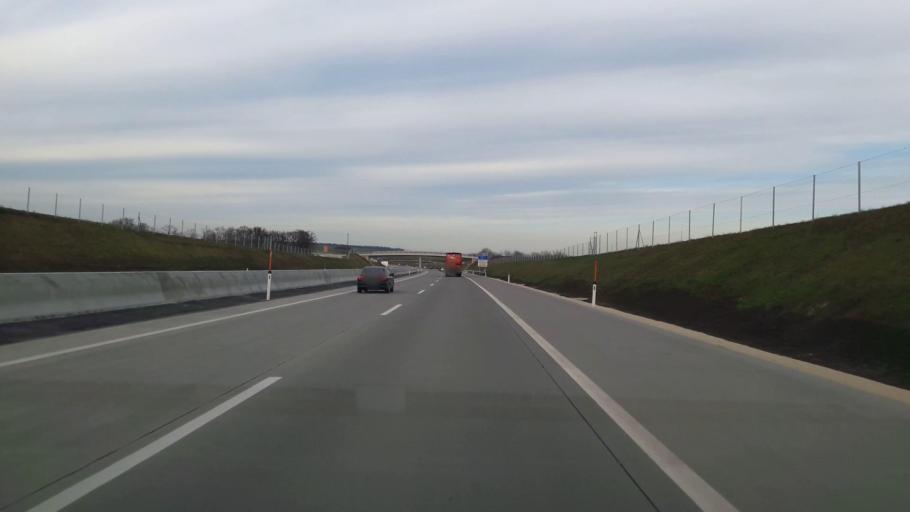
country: AT
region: Lower Austria
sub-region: Politischer Bezirk Mistelbach
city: Grosskrut
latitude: 48.6406
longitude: 16.6856
